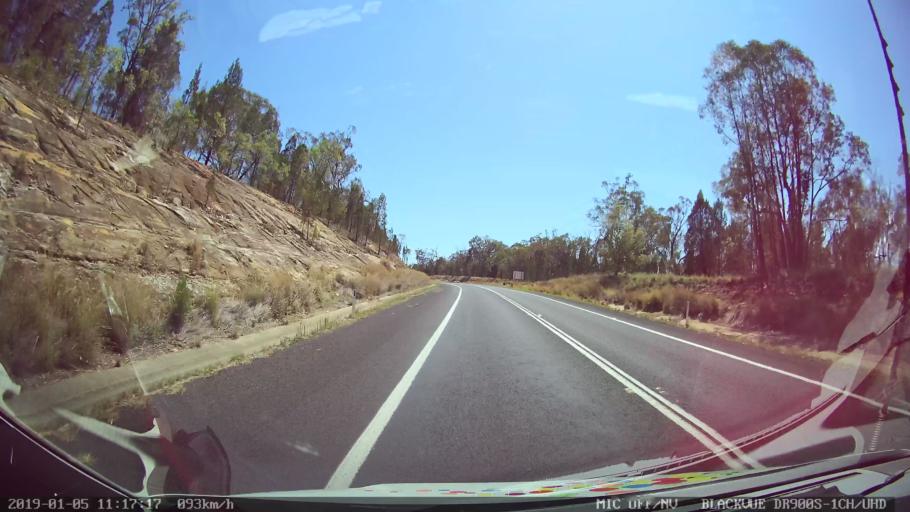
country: AU
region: New South Wales
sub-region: Warrumbungle Shire
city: Coonabarabran
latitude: -31.3283
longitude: 149.3056
